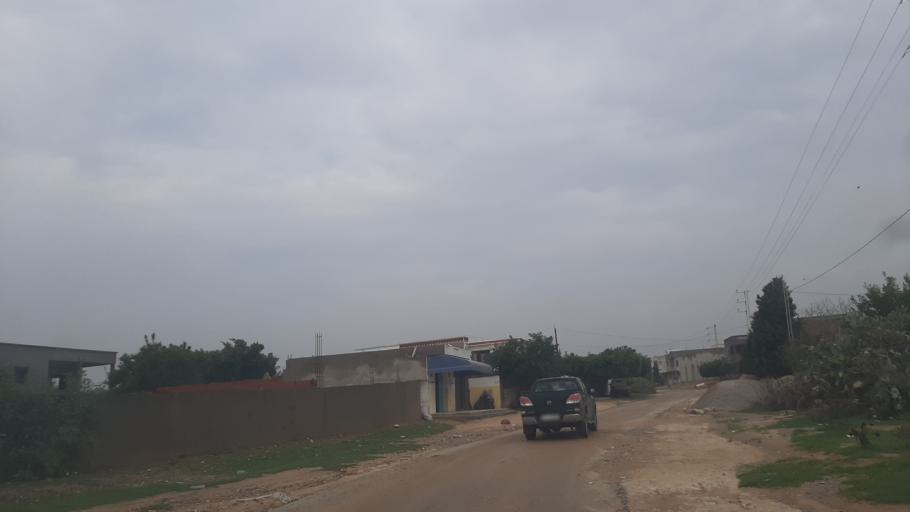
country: TN
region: Al Munastir
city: Sidi Bin Nur
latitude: 35.4763
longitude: 10.8752
